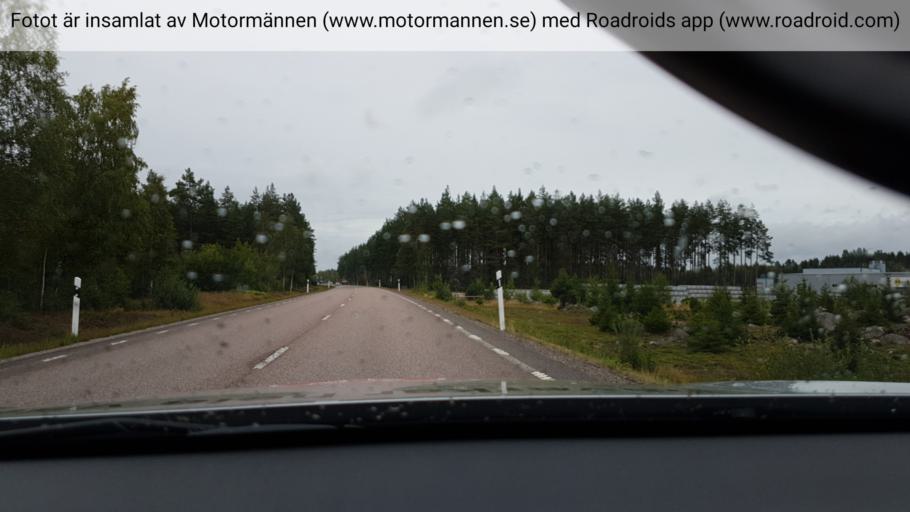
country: SE
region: Gaevleborg
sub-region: Gavle Kommun
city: Hedesunda
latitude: 60.3871
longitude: 16.9760
